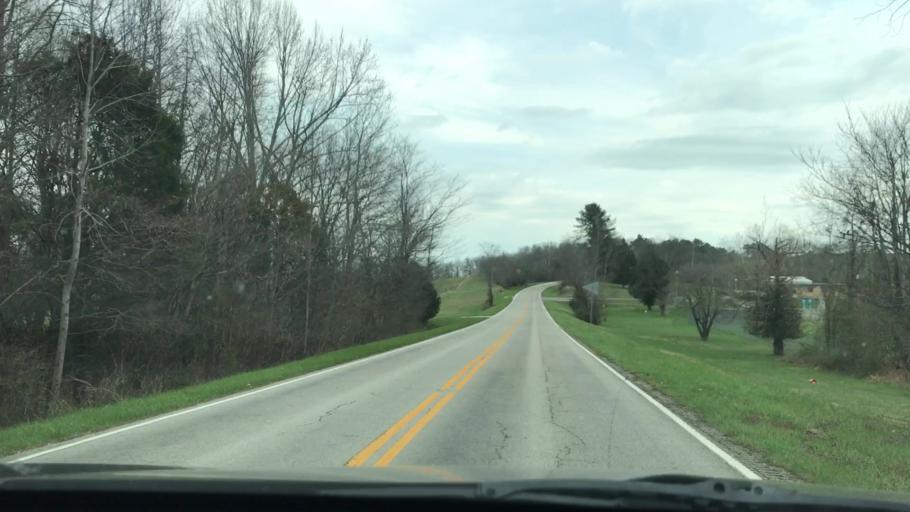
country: US
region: Kentucky
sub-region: Hart County
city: Munfordville
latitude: 37.3173
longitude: -85.7630
